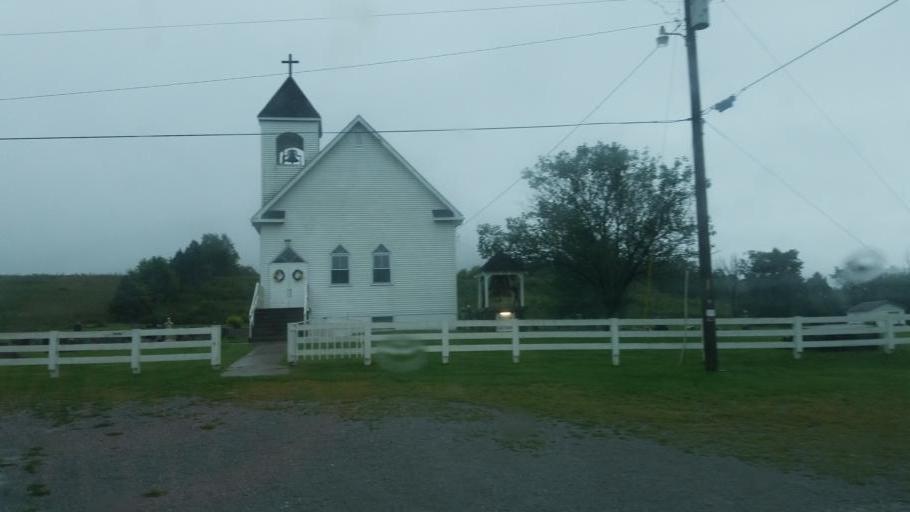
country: US
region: Kentucky
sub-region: Fleming County
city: Flemingsburg
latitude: 38.3623
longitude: -83.6146
